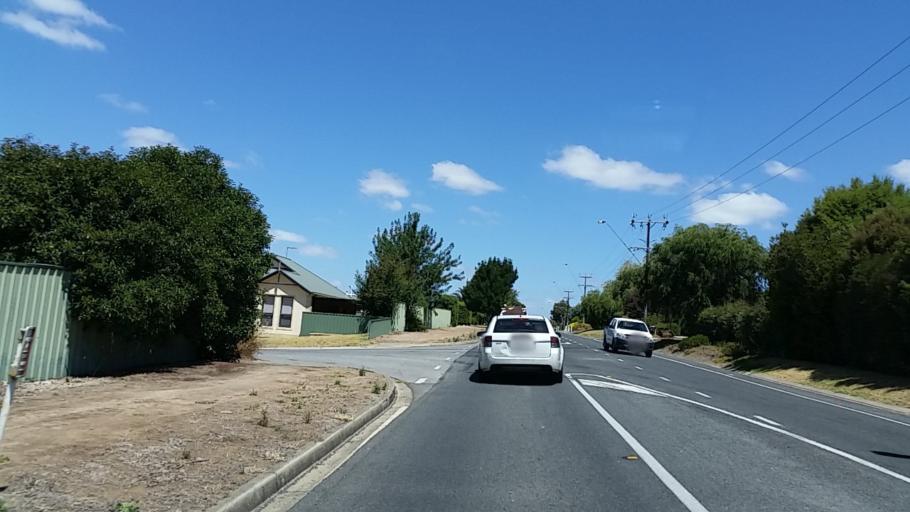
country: AU
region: South Australia
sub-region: Mount Barker
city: Nairne
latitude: -35.0266
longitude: 138.9020
